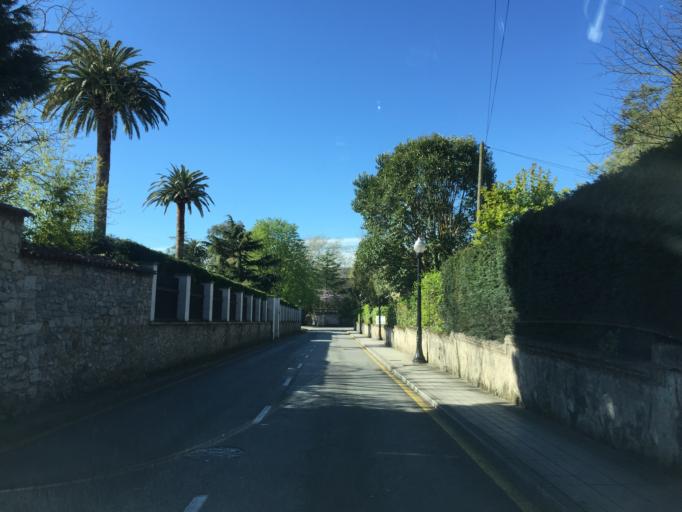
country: ES
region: Asturias
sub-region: Province of Asturias
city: Gijon
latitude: 43.5349
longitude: -5.6235
